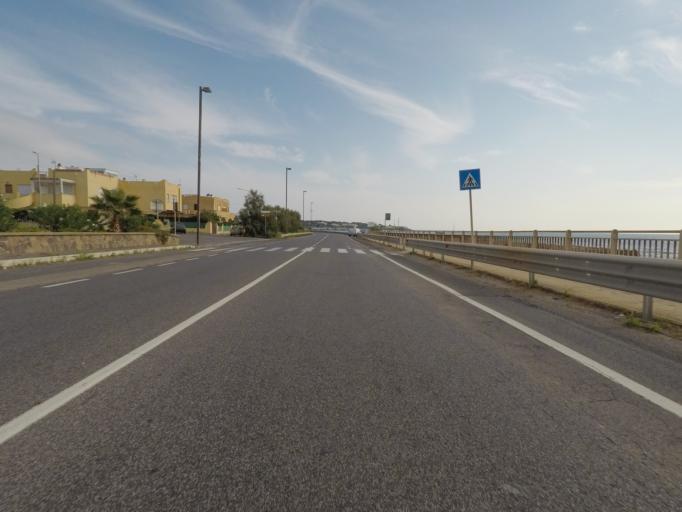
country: IT
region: Latium
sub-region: Citta metropolitana di Roma Capitale
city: Santa Marinella
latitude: 42.0426
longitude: 11.8277
